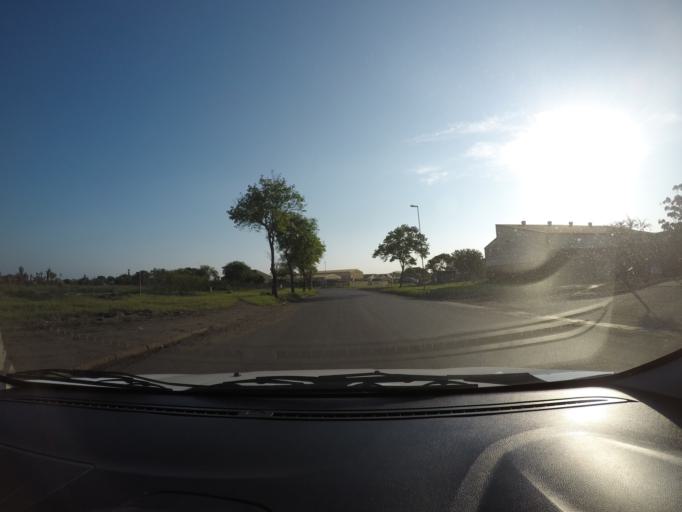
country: ZA
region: KwaZulu-Natal
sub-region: uThungulu District Municipality
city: Richards Bay
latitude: -28.7621
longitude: 32.0073
